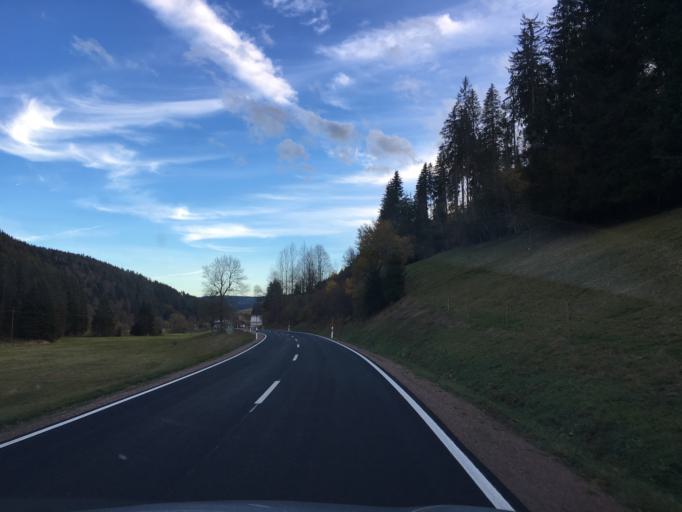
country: DE
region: Baden-Wuerttemberg
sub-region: Freiburg Region
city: Furtwangen im Schwarzwald
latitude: 48.0732
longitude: 8.1873
